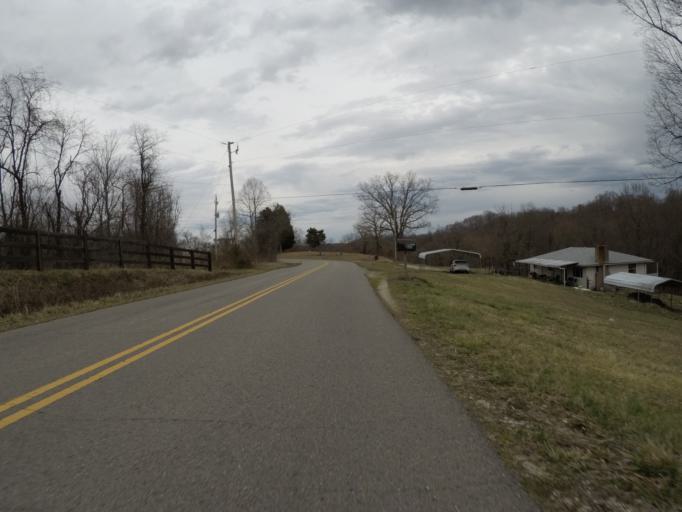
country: US
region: Ohio
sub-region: Lawrence County
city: Burlington
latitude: 38.4421
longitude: -82.5262
